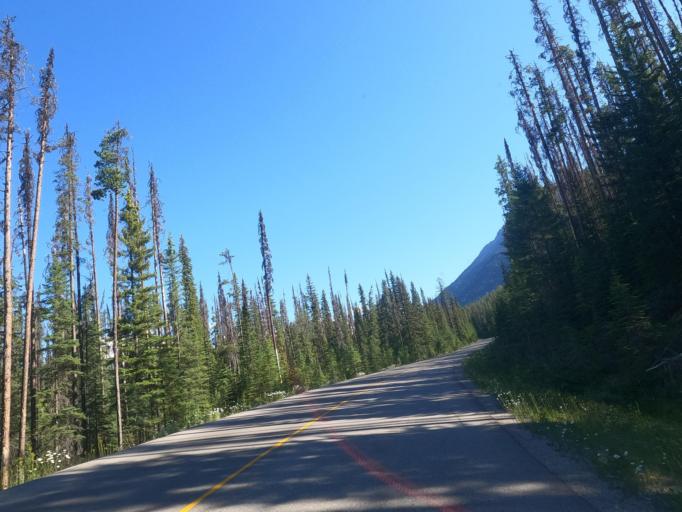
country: CA
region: Alberta
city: Lake Louise
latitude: 51.3878
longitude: -116.5377
